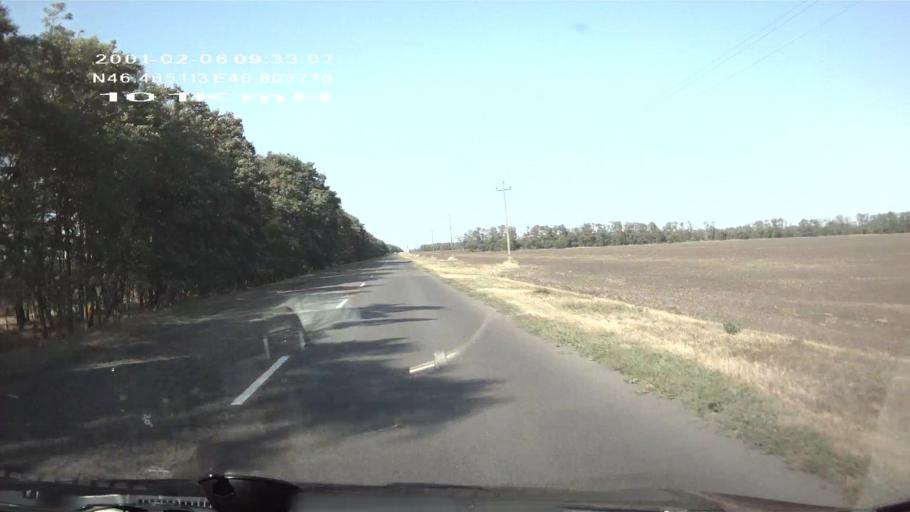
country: RU
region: Rostov
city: Yegorlykskaya
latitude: 46.4651
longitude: 40.8070
